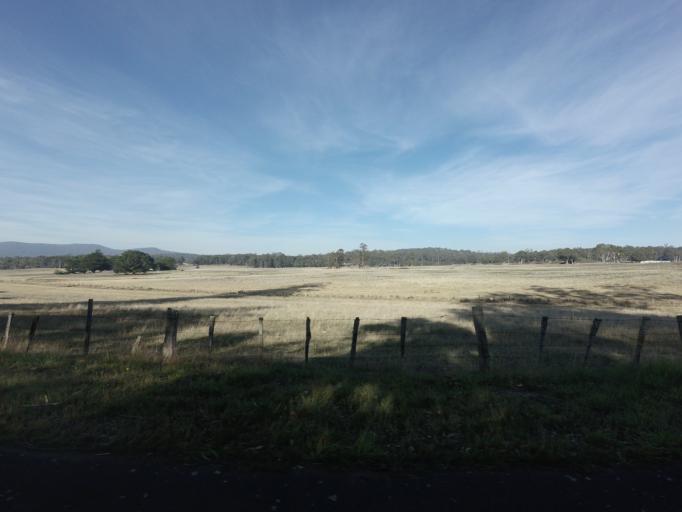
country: AU
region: Tasmania
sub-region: Sorell
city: Sorell
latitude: -42.4760
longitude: 147.4586
